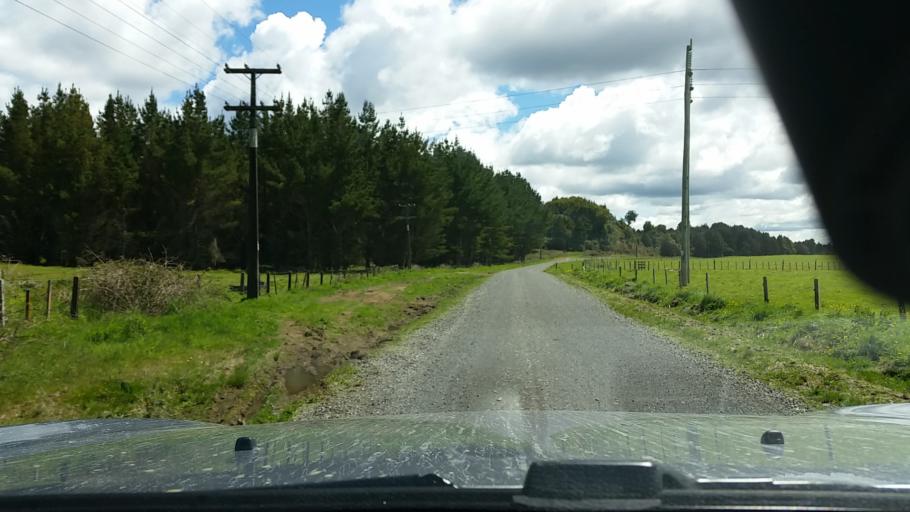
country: NZ
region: Bay of Plenty
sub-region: Rotorua District
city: Rotorua
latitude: -38.0822
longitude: 176.0452
